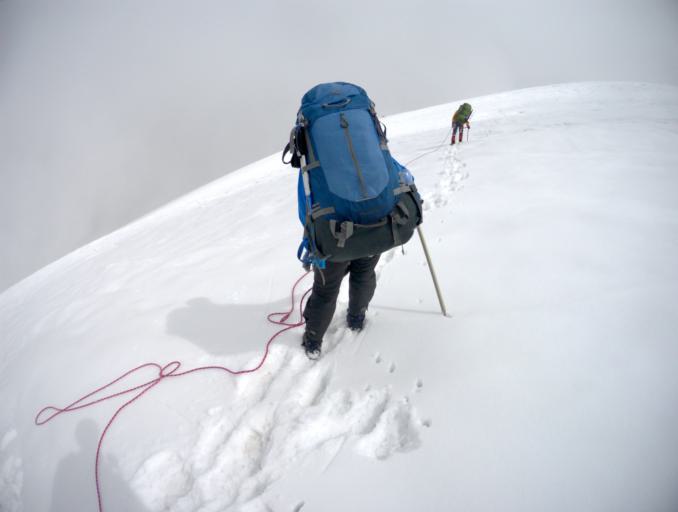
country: RU
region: Kabardino-Balkariya
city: Terskol
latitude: 43.3739
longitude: 42.4811
